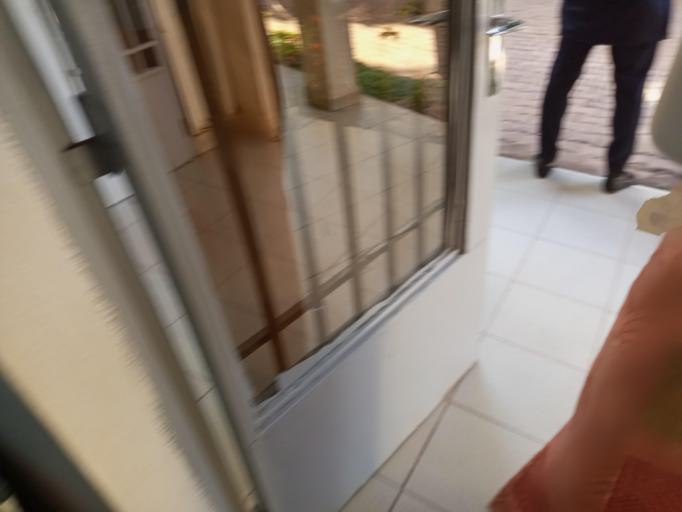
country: ML
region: Bamako
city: Bamako
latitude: 12.6592
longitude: -7.9967
